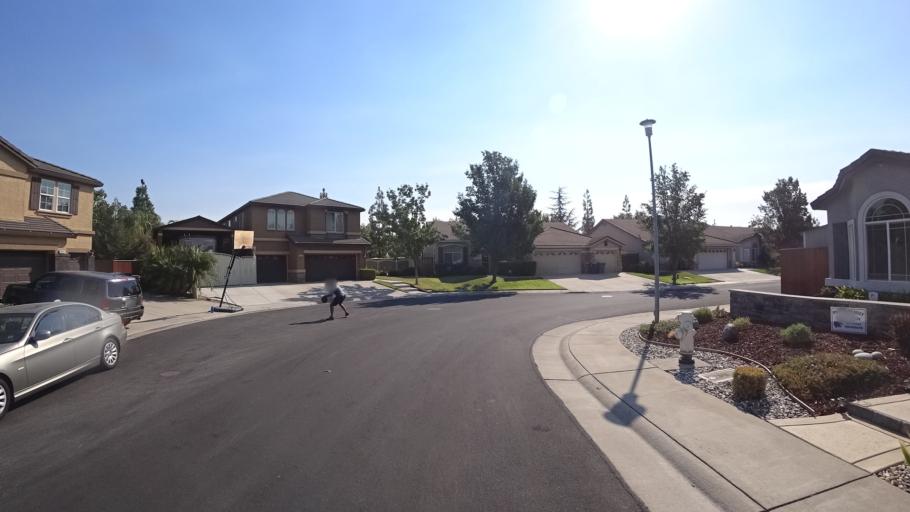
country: US
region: California
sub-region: Sacramento County
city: Laguna
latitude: 38.3854
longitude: -121.4345
